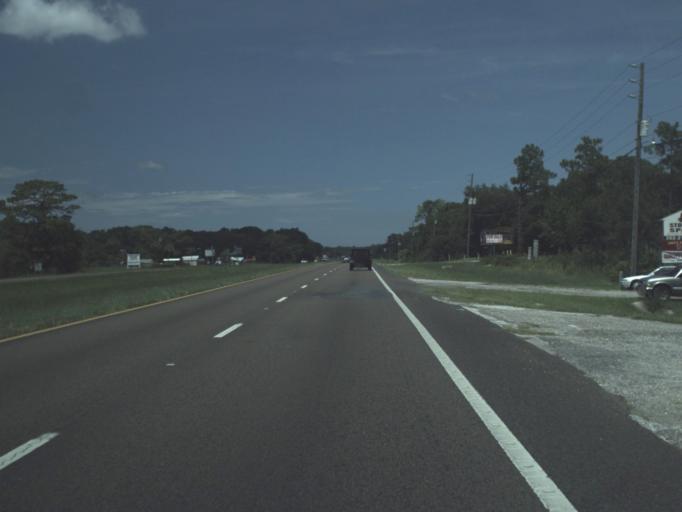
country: US
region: Florida
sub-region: Citrus County
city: Homosassa Springs
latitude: 28.7838
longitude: -82.5601
